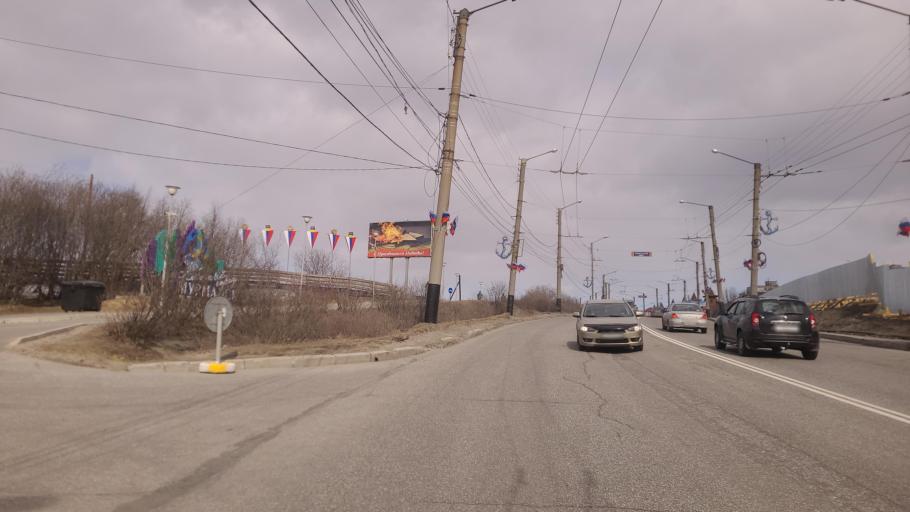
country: RU
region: Murmansk
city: Murmansk
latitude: 68.9872
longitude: 33.0916
